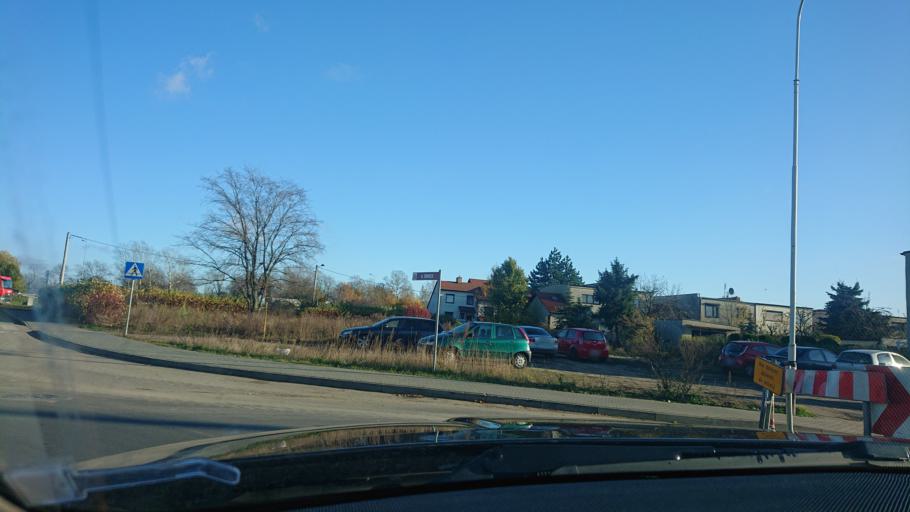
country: PL
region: Greater Poland Voivodeship
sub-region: Powiat gnieznienski
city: Gniezno
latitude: 52.5286
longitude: 17.5818
